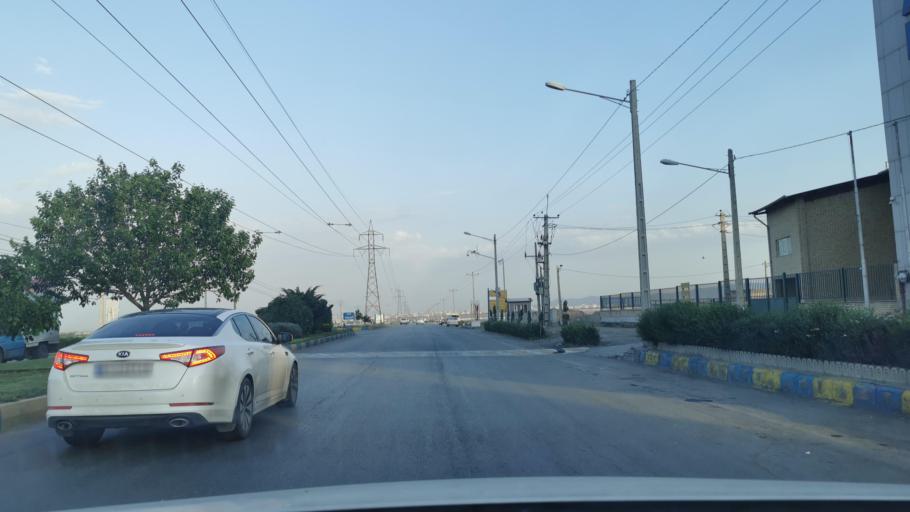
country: IR
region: Razavi Khorasan
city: Torqabeh
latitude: 36.4225
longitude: 59.4266
